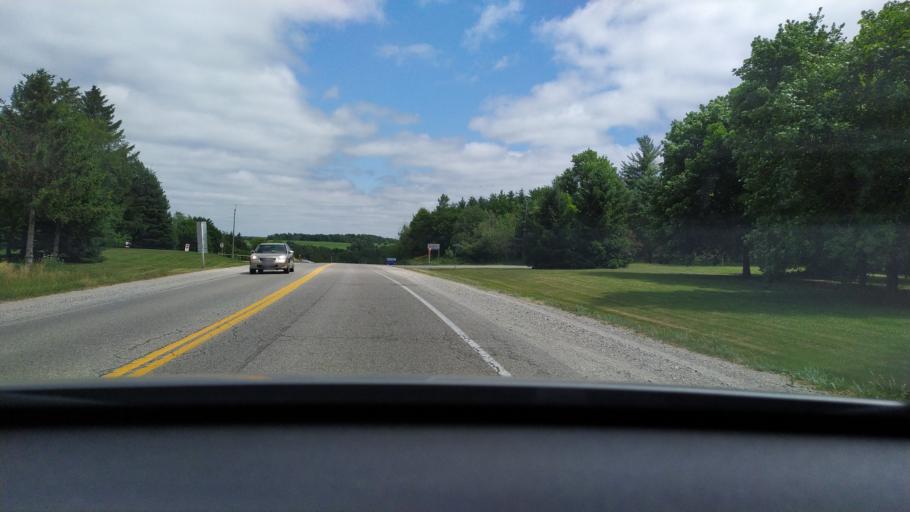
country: CA
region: Ontario
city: Stratford
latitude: 43.2827
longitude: -80.9654
